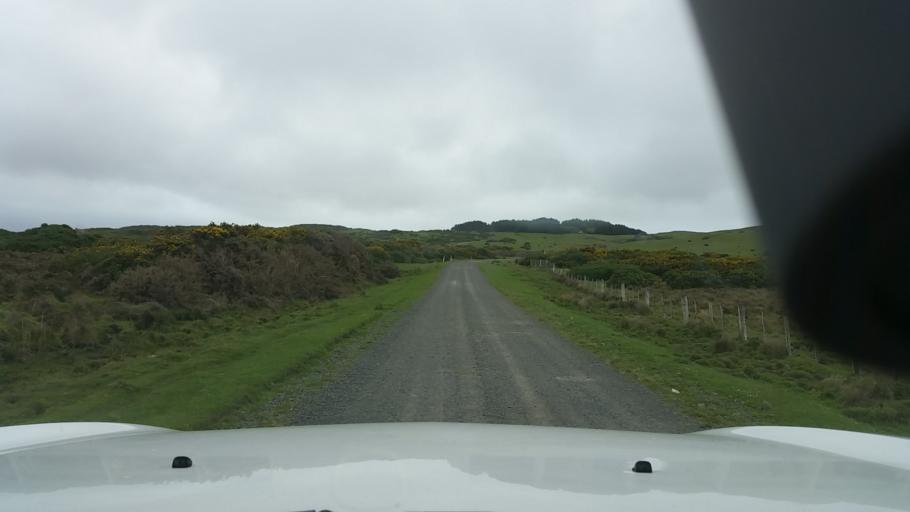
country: NZ
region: Chatham Islands
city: Waitangi
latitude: -43.7338
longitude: -176.5701
